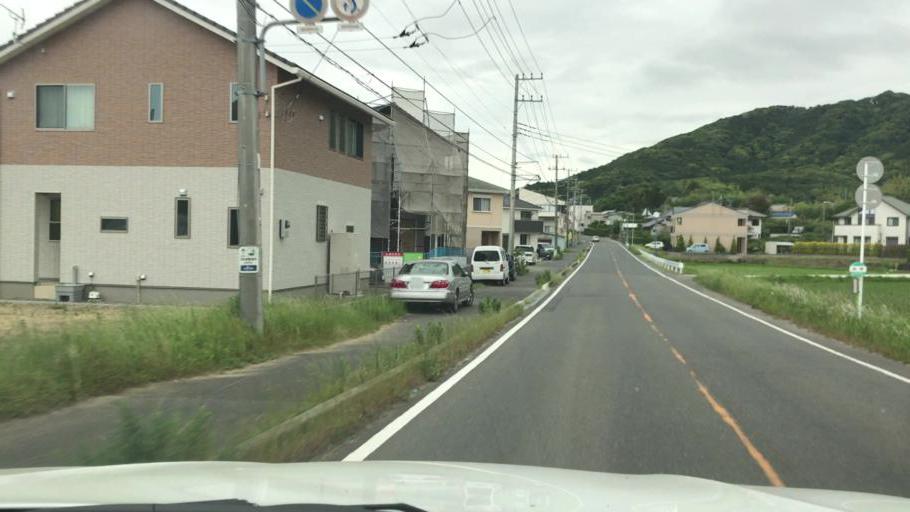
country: JP
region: Chiba
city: Kawaguchi
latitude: 35.1223
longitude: 140.0971
